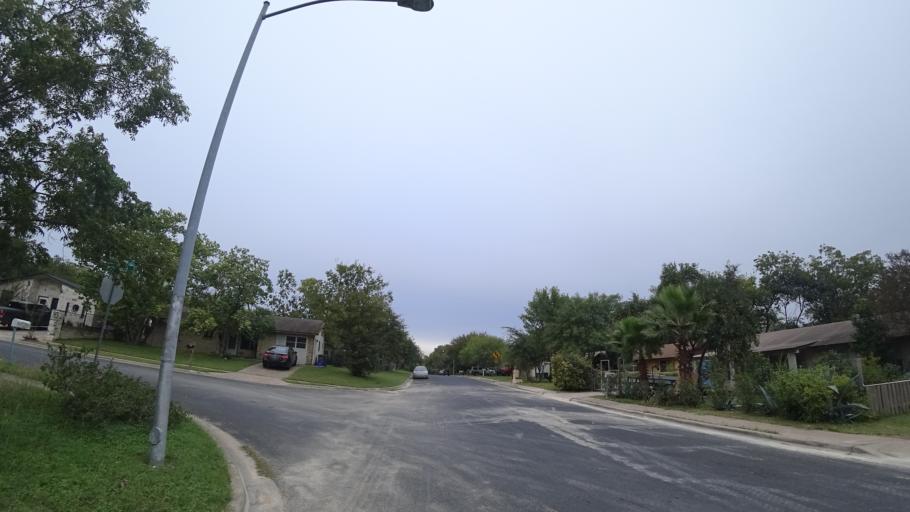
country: US
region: Texas
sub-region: Travis County
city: Onion Creek
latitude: 30.2055
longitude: -97.7780
